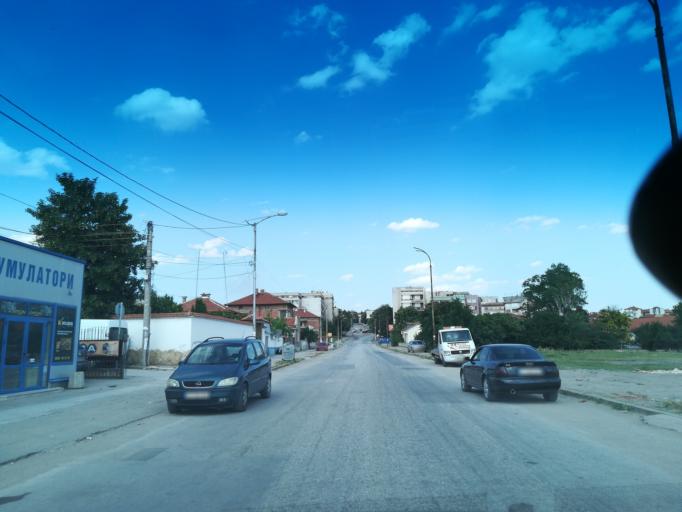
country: BG
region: Stara Zagora
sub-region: Obshtina Chirpan
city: Chirpan
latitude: 42.1979
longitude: 25.3194
